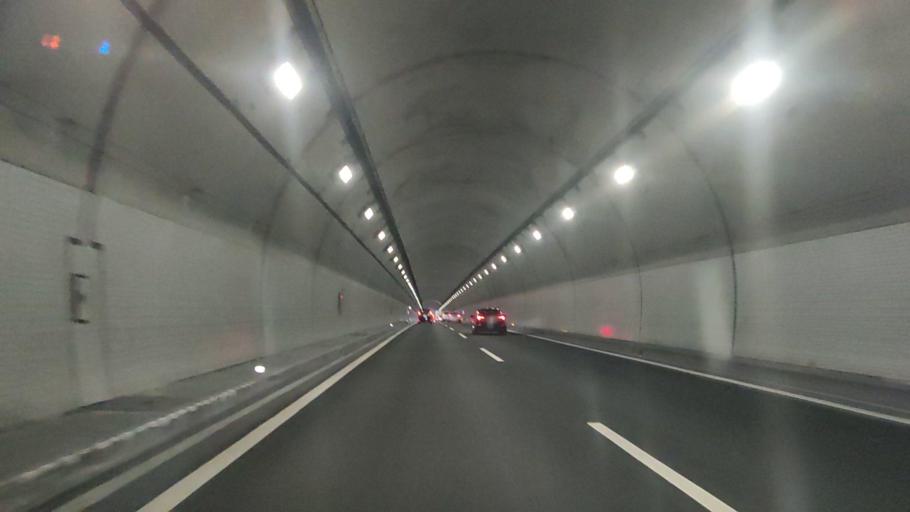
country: JP
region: Fukuoka
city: Kanda
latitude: 33.8094
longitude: 130.9142
